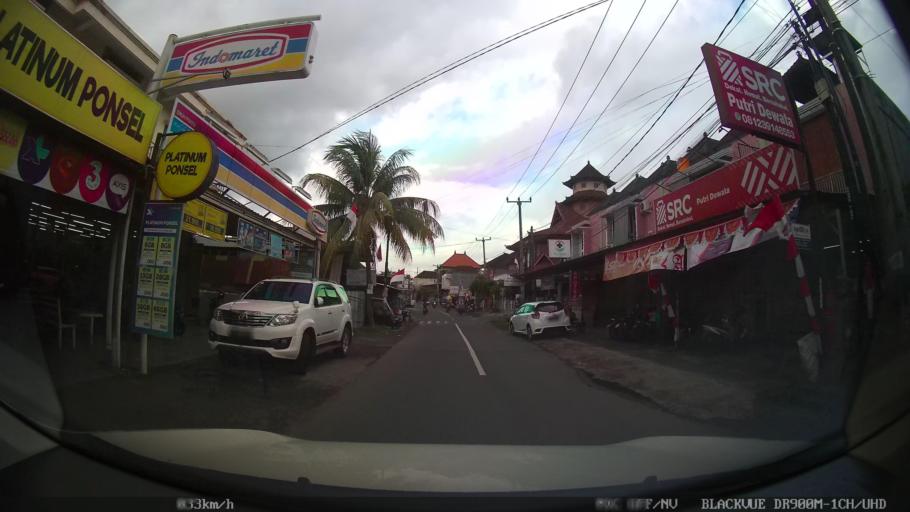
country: ID
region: Bali
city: Banjar Tegal Belodan
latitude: -8.5454
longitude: 115.1206
